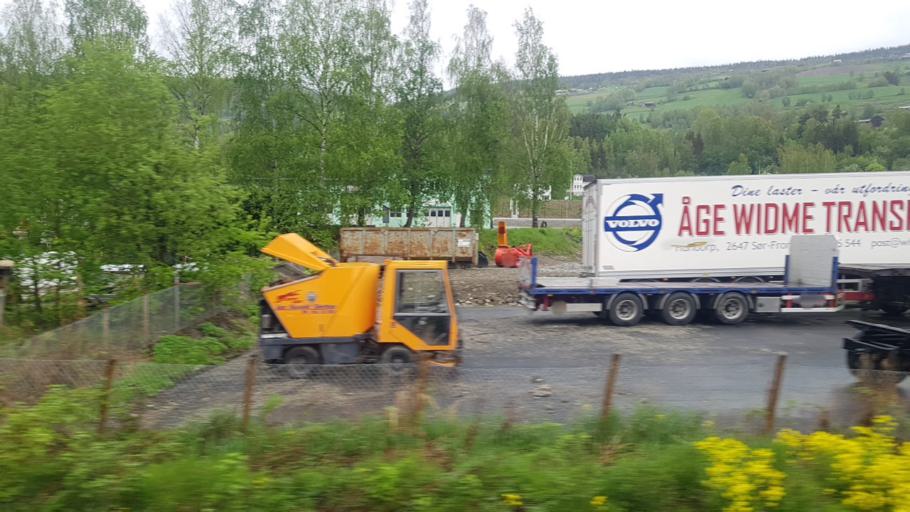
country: NO
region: Oppland
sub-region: Sor-Fron
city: Hundorp
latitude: 61.5631
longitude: 9.9230
